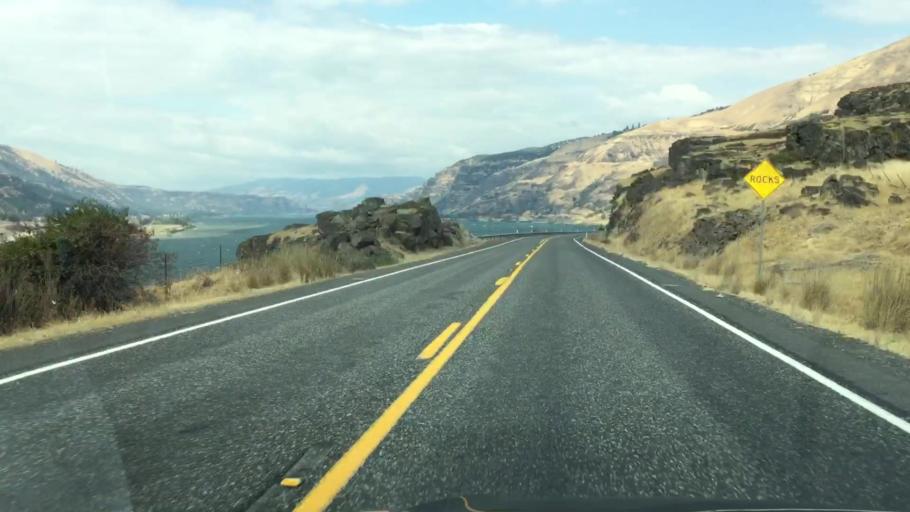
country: US
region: Washington
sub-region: Klickitat County
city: Dallesport
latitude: 45.6624
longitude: -121.1997
